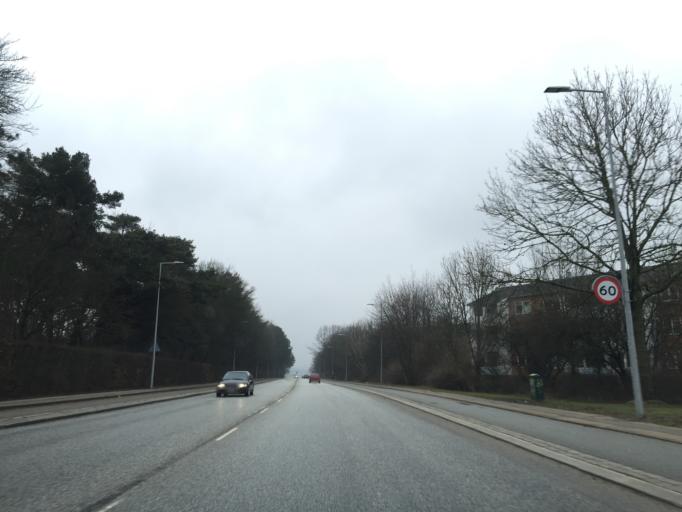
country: DK
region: South Denmark
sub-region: Kolding Kommune
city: Kolding
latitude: 55.4760
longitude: 9.4802
